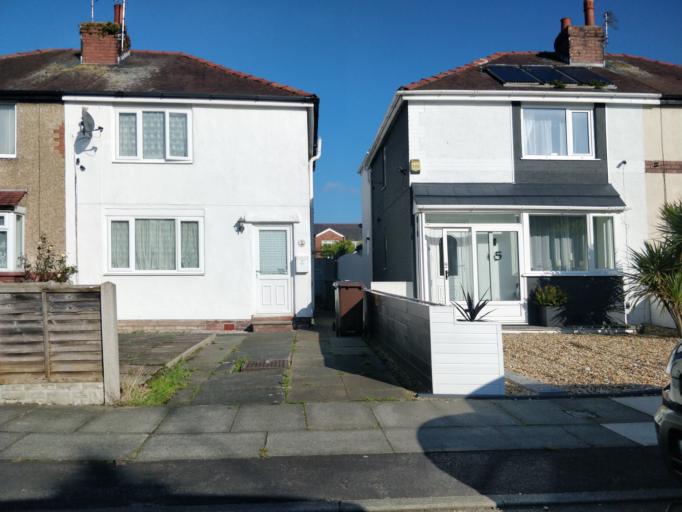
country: GB
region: England
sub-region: Lancashire
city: Banks
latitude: 53.6699
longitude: -2.9522
